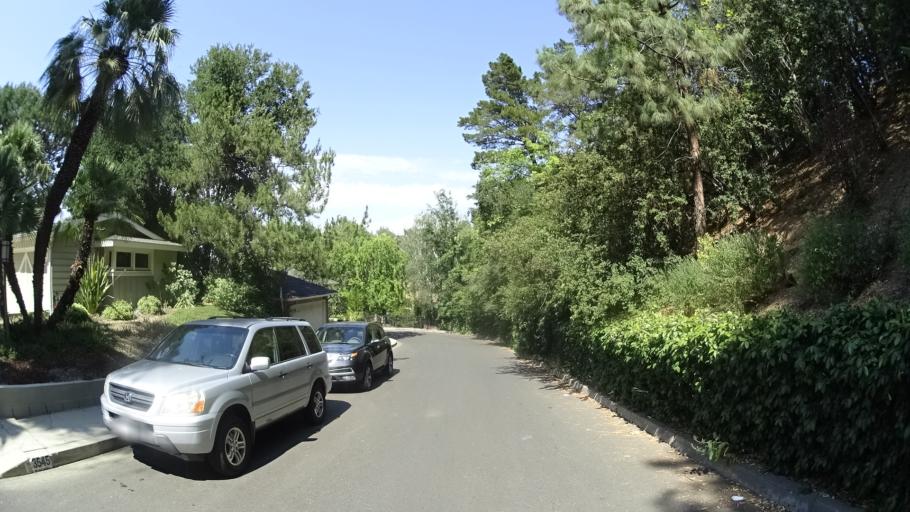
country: US
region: California
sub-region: Los Angeles County
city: North Hollywood
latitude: 34.1353
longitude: -118.3939
